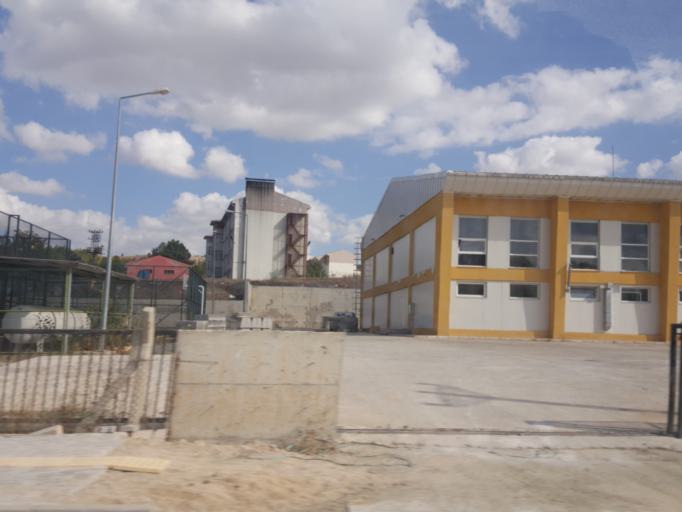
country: TR
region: Tokat
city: Artova
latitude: 40.1102
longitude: 36.3046
